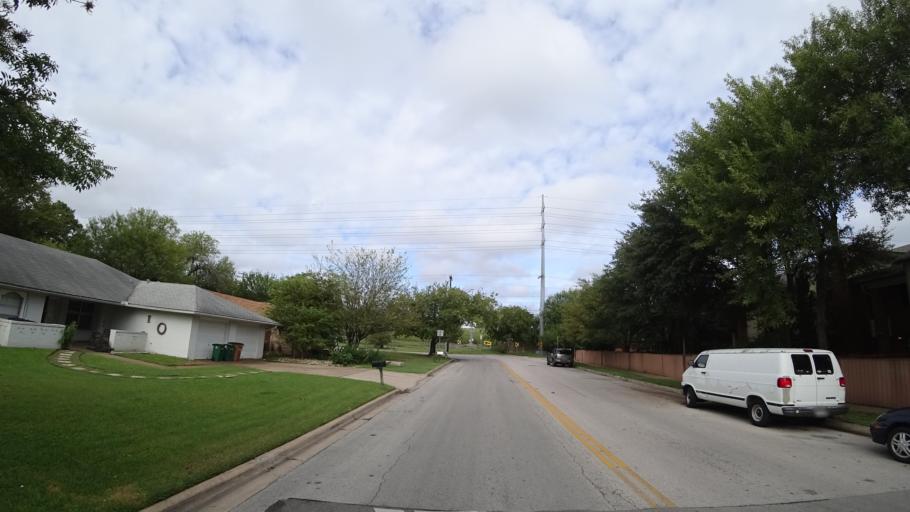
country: US
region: Texas
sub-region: Travis County
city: West Lake Hills
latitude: 30.3595
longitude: -97.7433
